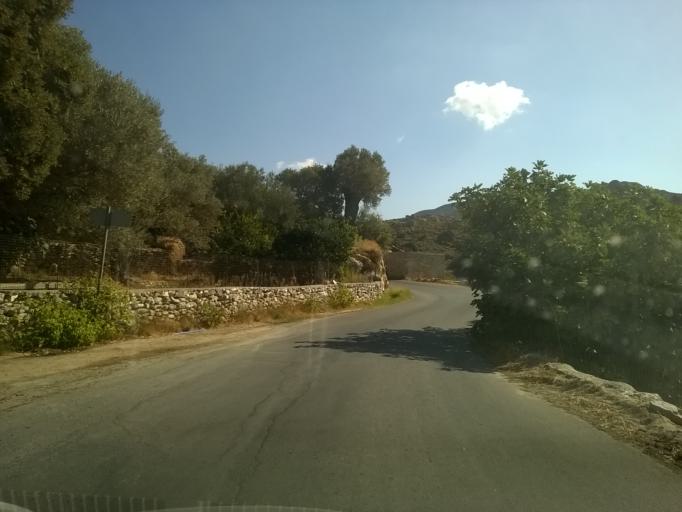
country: GR
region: South Aegean
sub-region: Nomos Kykladon
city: Filotion
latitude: 37.1003
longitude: 25.4828
